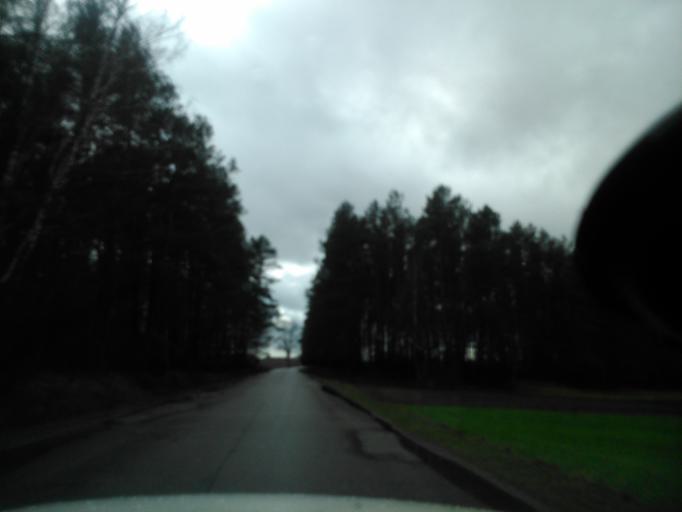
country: PL
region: Warmian-Masurian Voivodeship
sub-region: Powiat dzialdowski
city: Lidzbark
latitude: 53.2798
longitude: 19.8443
